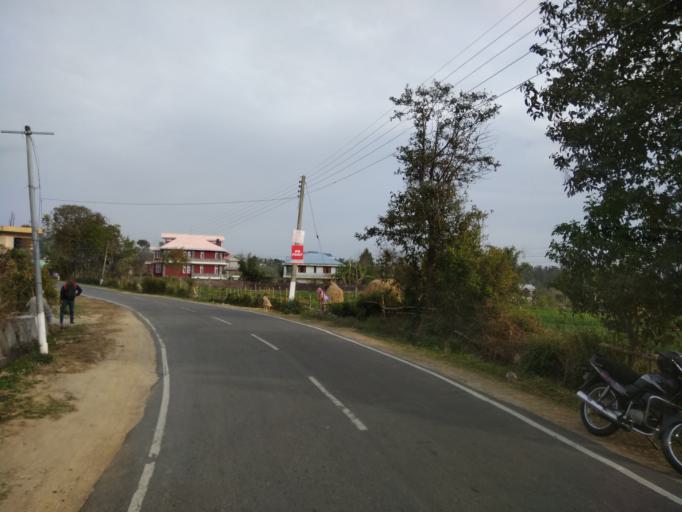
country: IN
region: Himachal Pradesh
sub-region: Kangra
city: Palampur
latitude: 32.1100
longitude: 76.4935
